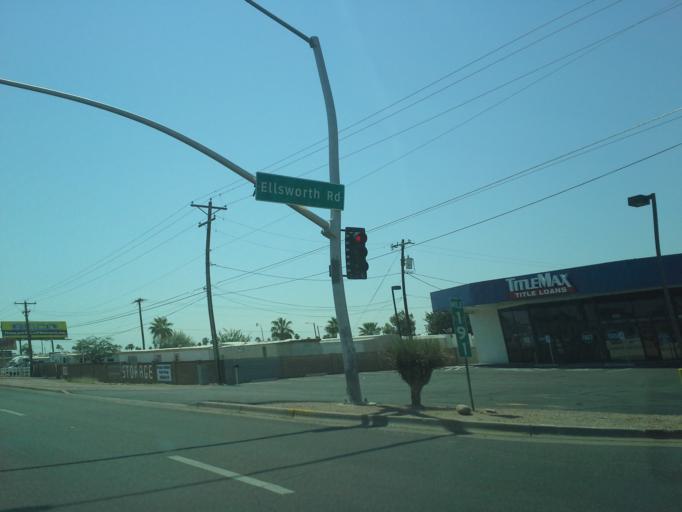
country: US
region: Arizona
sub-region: Pinal County
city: Apache Junction
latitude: 33.4151
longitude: -111.6326
